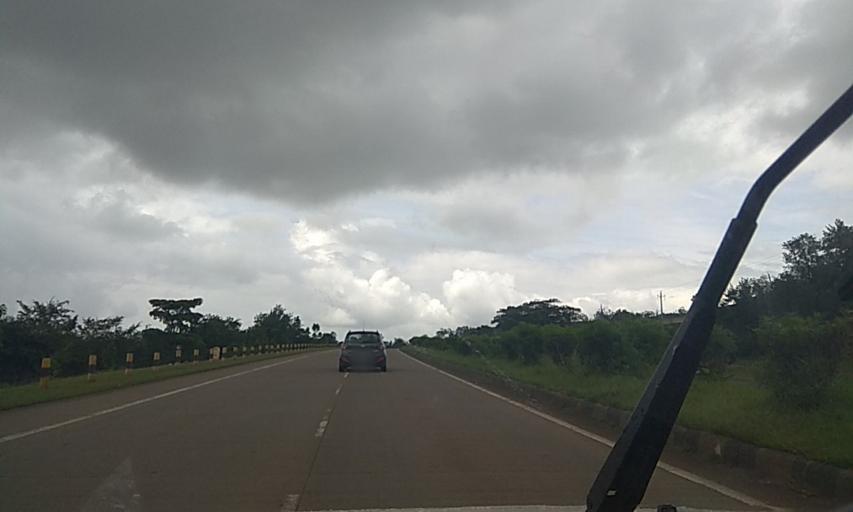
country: IN
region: Karnataka
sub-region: Belgaum
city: Sankeshwar
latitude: 16.2824
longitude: 74.4463
